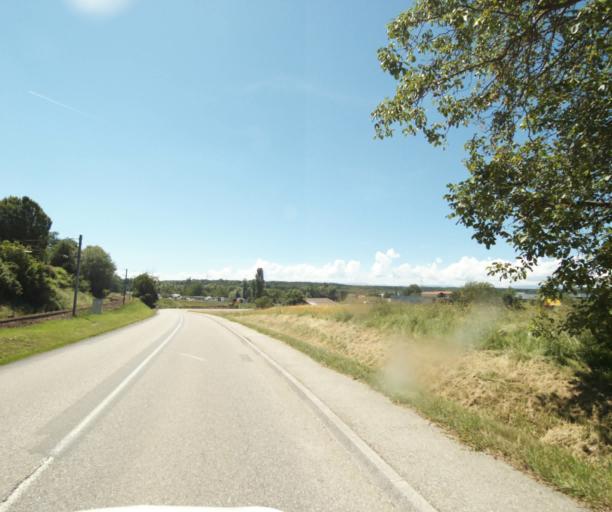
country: FR
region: Rhone-Alpes
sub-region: Departement de la Haute-Savoie
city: Bons-en-Chablais
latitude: 46.2715
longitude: 6.3555
